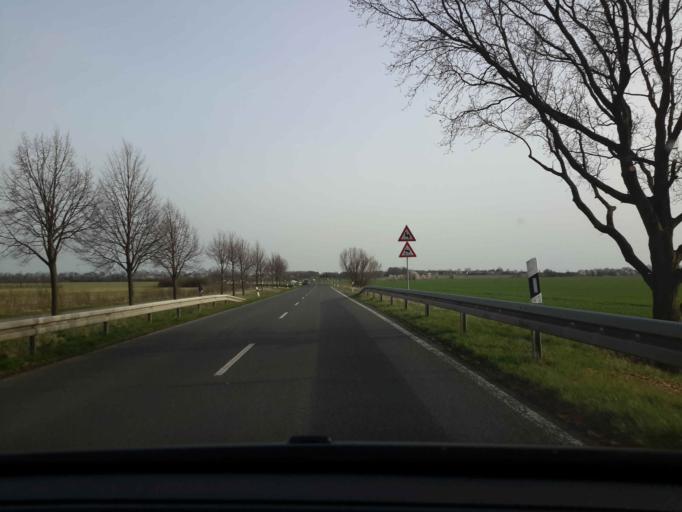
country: DE
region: Saxony
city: Rackwitz
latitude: 51.4226
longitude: 12.3577
